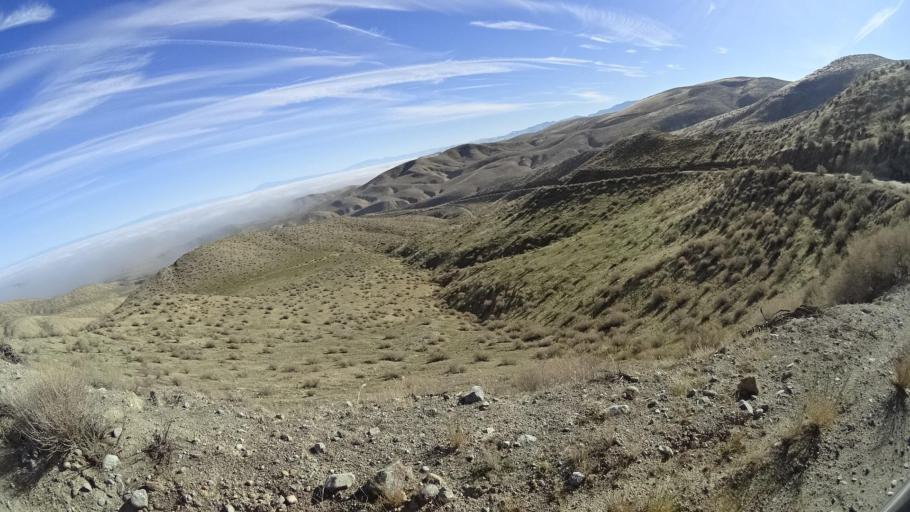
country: US
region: California
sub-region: Kern County
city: Maricopa
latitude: 35.0115
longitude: -119.4633
